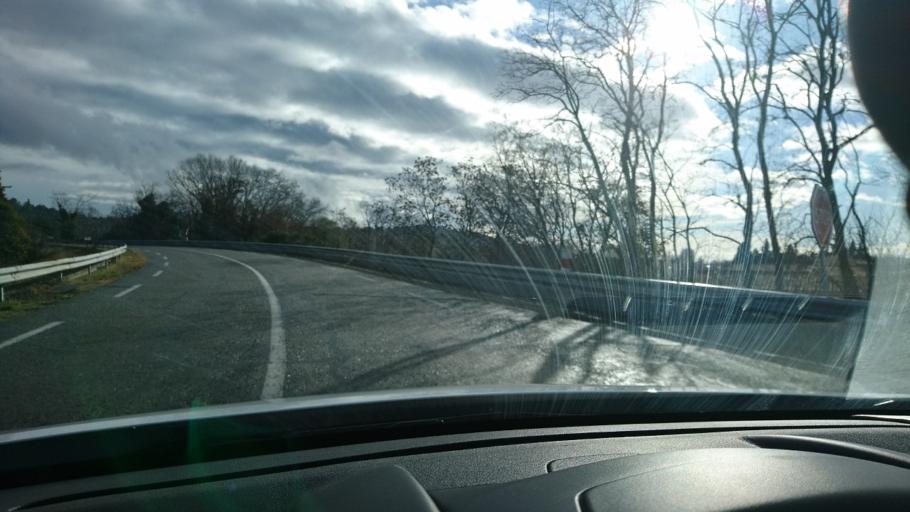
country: FR
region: Provence-Alpes-Cote d'Azur
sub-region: Departement du Vaucluse
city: Mondragon
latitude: 44.2412
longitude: 4.7057
